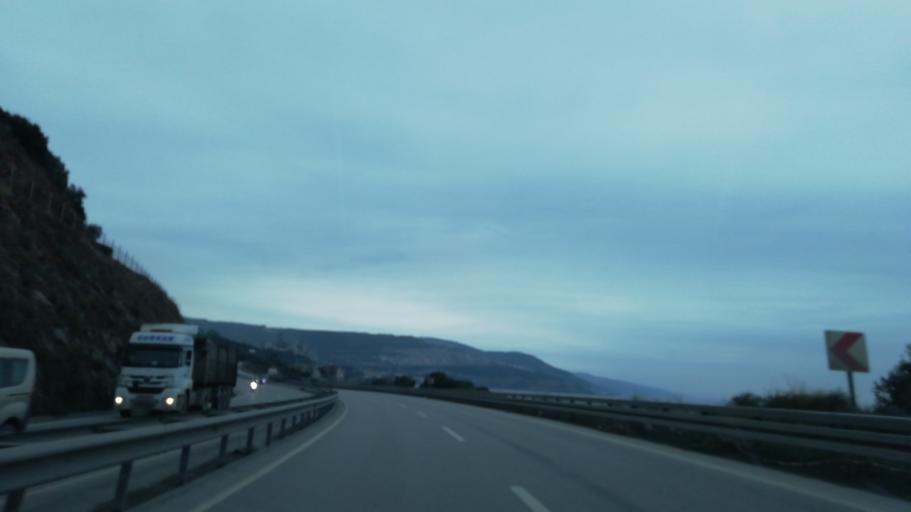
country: TR
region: Kocaeli
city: Tavsancil
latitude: 40.7691
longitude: 29.5790
